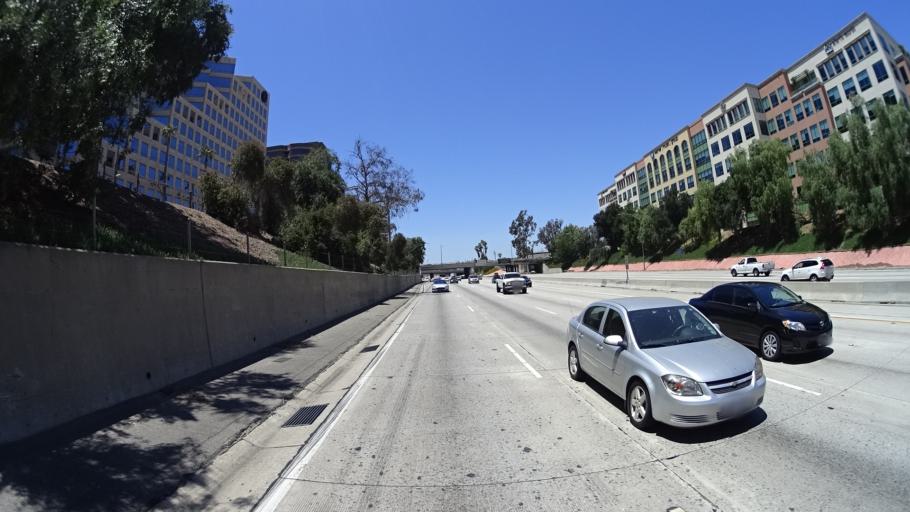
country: US
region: California
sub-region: Los Angeles County
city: Universal City
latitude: 34.1526
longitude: -118.3358
